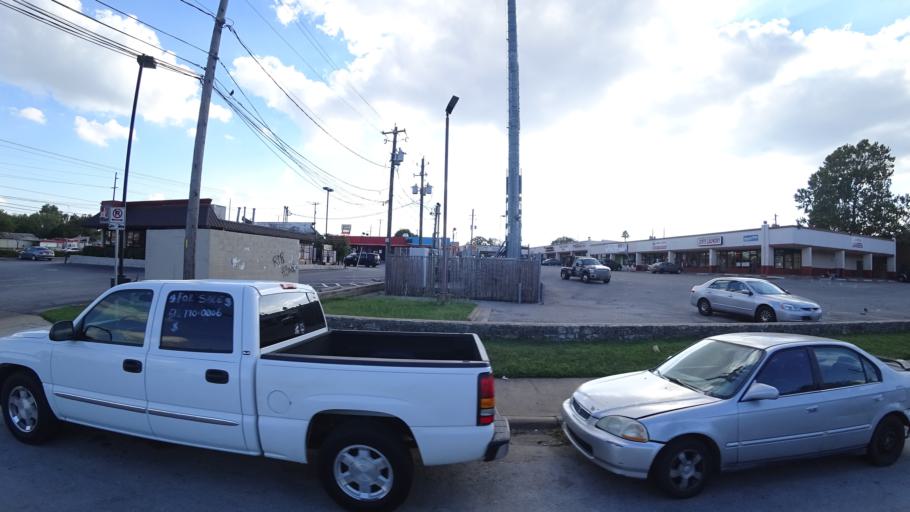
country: US
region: Texas
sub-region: Travis County
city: Wells Branch
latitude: 30.3560
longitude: -97.7032
